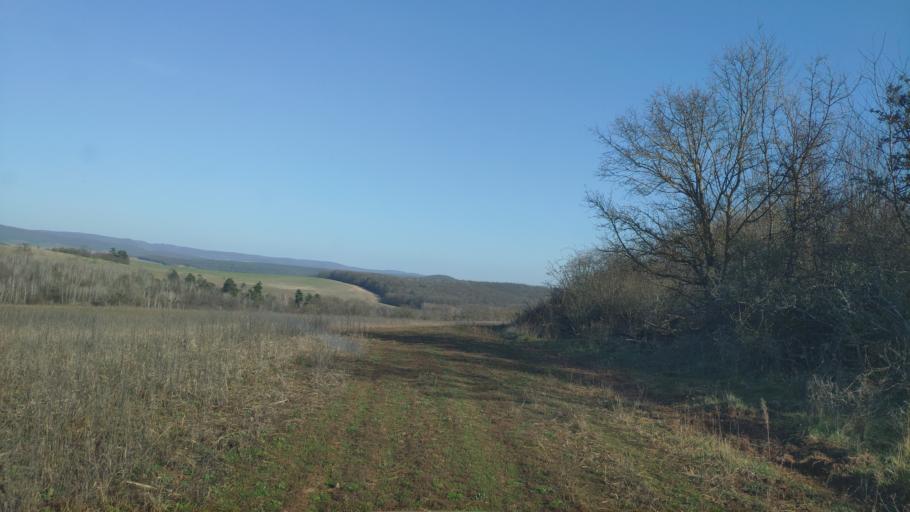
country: SK
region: Banskobystricky
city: Revuca
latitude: 48.5489
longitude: 20.2526
